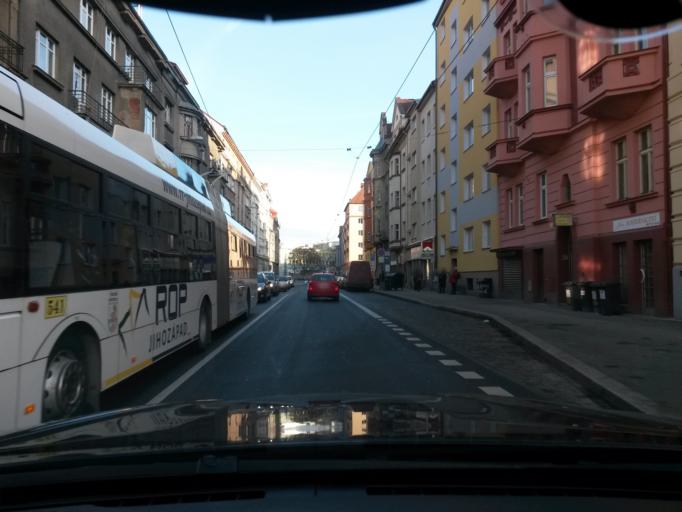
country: CZ
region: Plzensky
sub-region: Okres Plzen-Mesto
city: Pilsen
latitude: 49.7349
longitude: 13.3706
